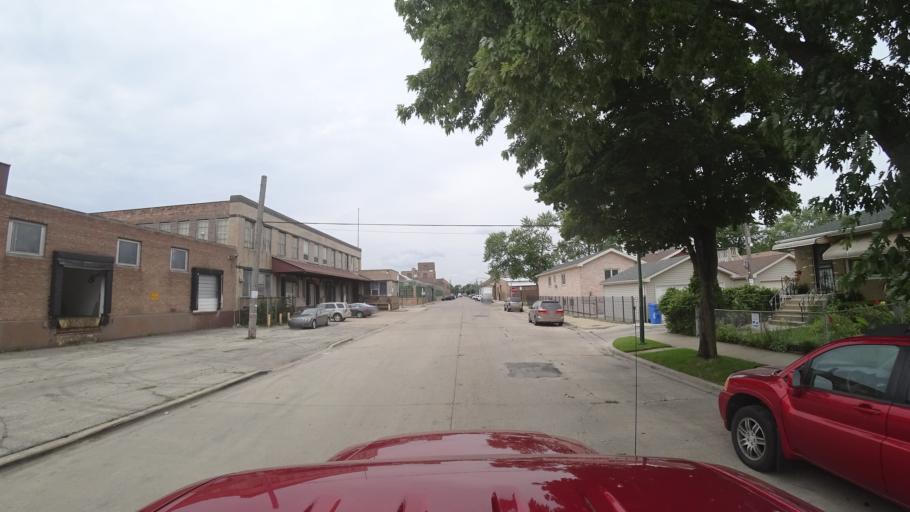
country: US
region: Illinois
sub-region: Cook County
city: Chicago
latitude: 41.8274
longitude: -87.6915
